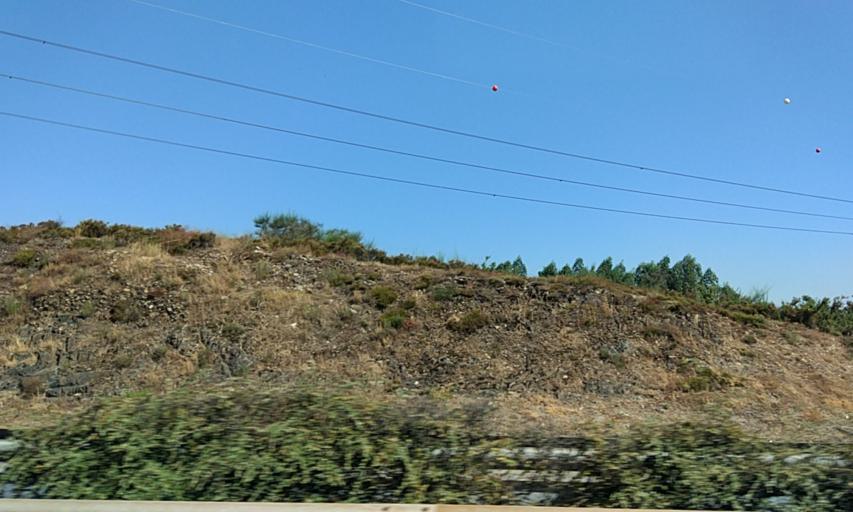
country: PT
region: Porto
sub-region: Paredes
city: Recarei
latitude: 41.1720
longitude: -8.4289
